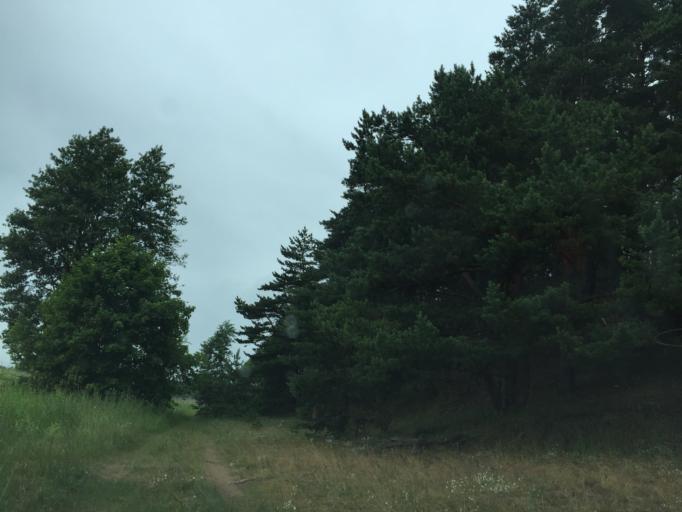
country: LV
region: Riga
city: Jaunciems
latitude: 57.0104
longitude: 24.2110
